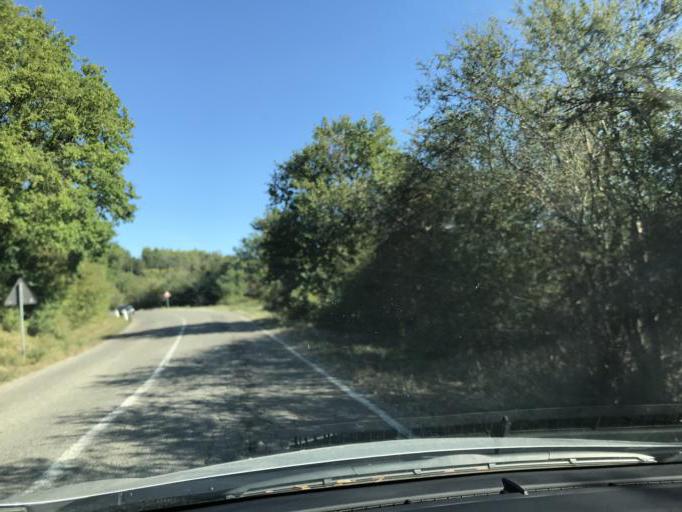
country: IT
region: Umbria
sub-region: Provincia di Terni
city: Avigliano Umbro
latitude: 42.6088
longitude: 12.4356
